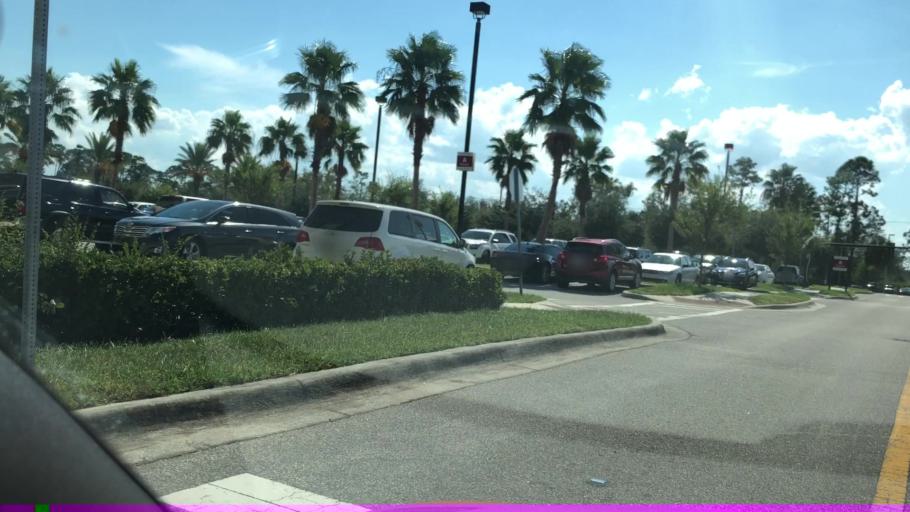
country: US
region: Florida
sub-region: Volusia County
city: Daytona Beach
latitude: 29.2031
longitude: -81.0551
